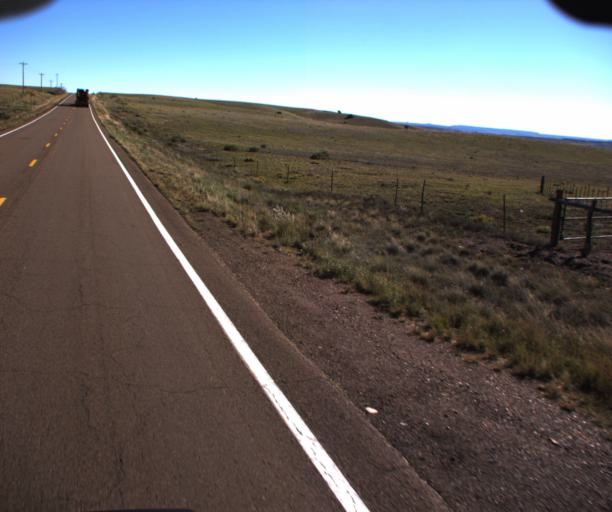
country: US
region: Arizona
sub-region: Apache County
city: Saint Johns
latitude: 34.5043
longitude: -109.4829
